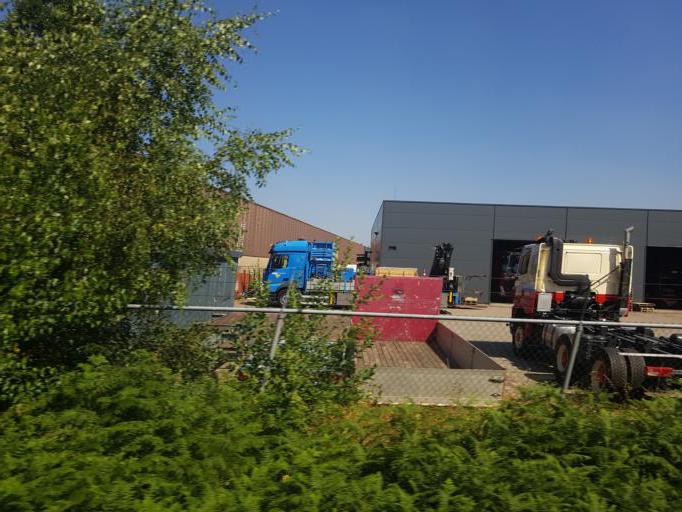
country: NL
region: Gelderland
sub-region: Gemeente Barneveld
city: Barneveld
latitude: 52.1619
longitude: 5.5851
